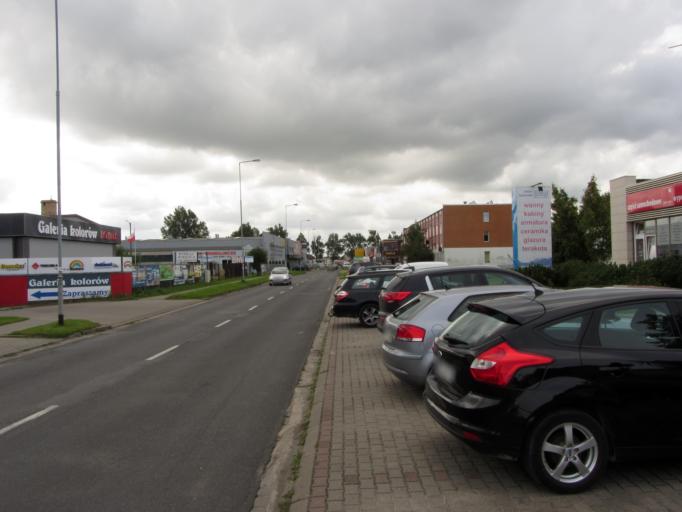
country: PL
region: West Pomeranian Voivodeship
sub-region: Powiat kolobrzeski
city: Kolobrzeg
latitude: 54.1677
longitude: 15.5492
